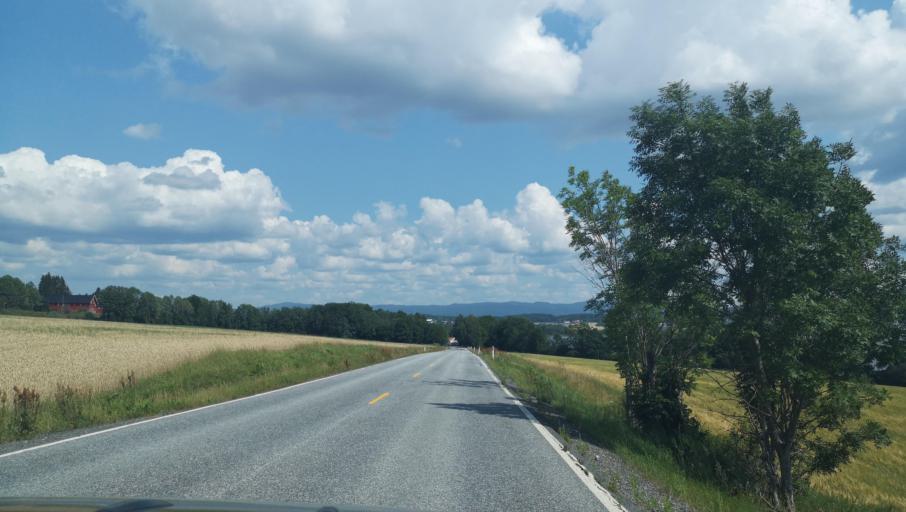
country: NO
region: Buskerud
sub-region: Ovre Eiker
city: Hokksund
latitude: 59.7064
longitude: 9.8112
